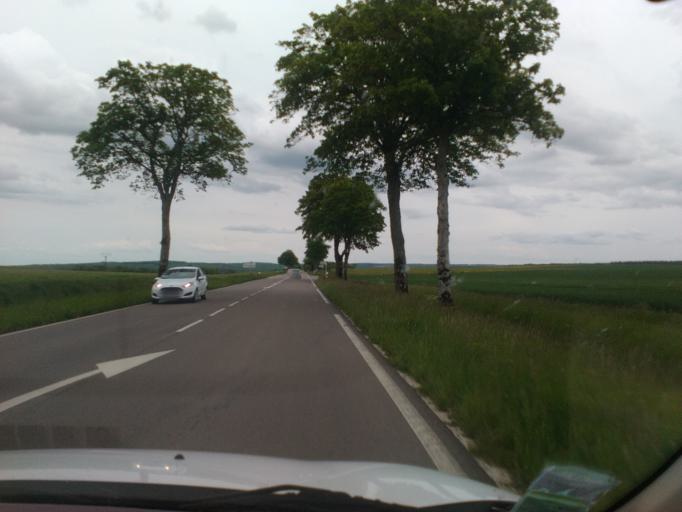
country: FR
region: Champagne-Ardenne
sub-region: Departement de l'Aube
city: Vendeuvre-sur-Barse
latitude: 48.2561
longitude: 4.5814
